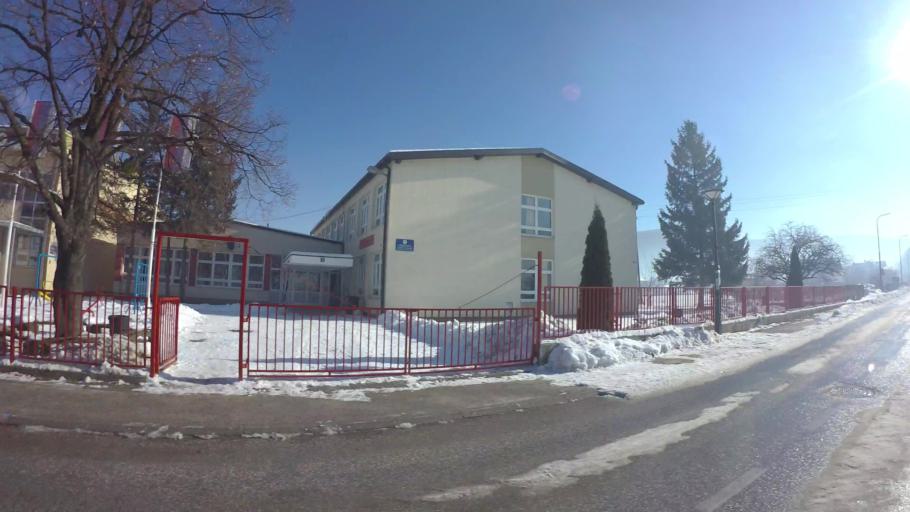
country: BA
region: Federation of Bosnia and Herzegovina
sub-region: Kanton Sarajevo
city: Sarajevo
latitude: 43.7935
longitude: 18.3531
